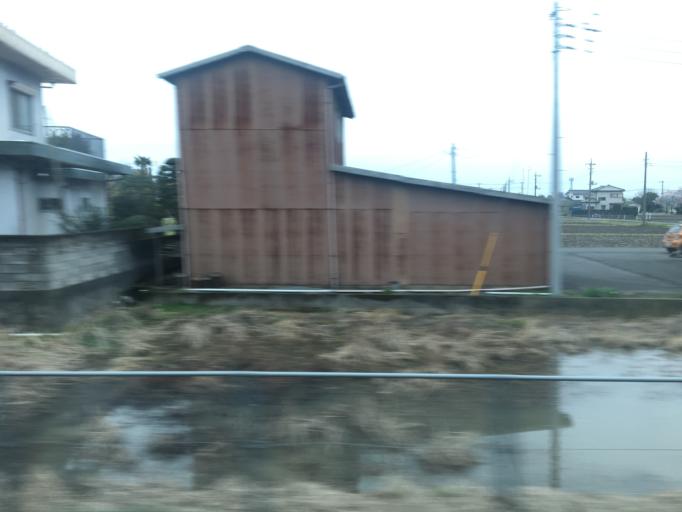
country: JP
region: Saitama
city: Kawagoe
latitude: 35.9019
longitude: 139.5041
